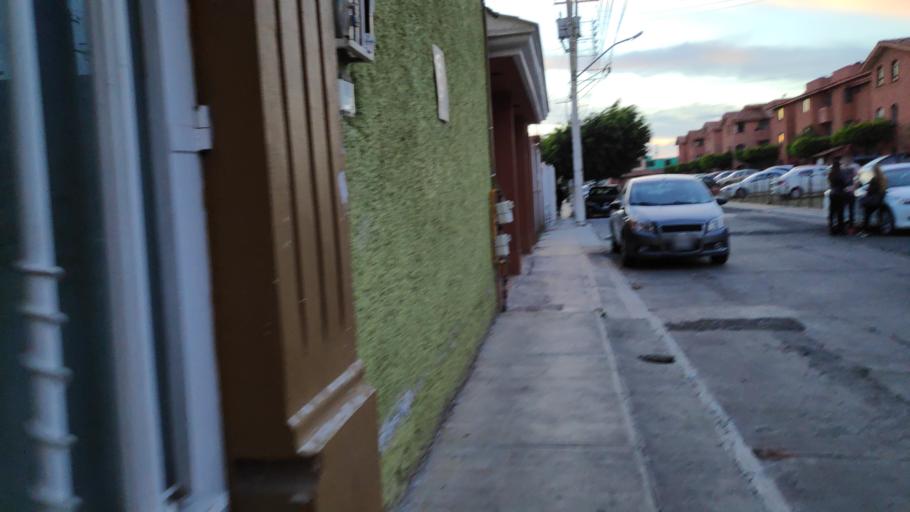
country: MX
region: Queretaro
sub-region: Queretaro
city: Santiago de Queretaro
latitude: 20.5827
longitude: -100.3813
